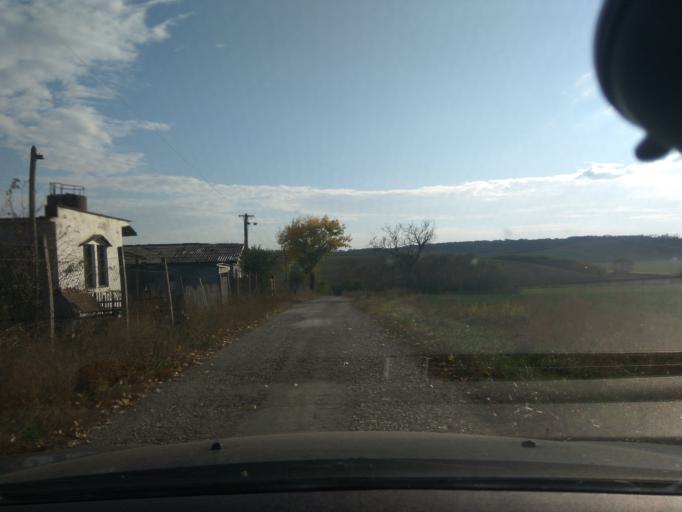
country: SK
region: Trnavsky
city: Hlohovec
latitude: 48.4459
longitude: 17.9257
